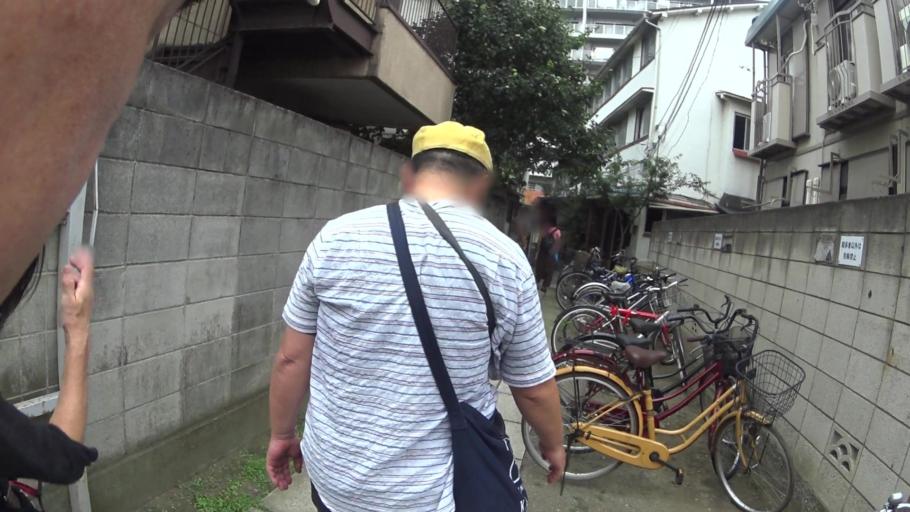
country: JP
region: Kanagawa
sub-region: Kawasaki-shi
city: Kawasaki
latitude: 35.5248
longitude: 139.6914
